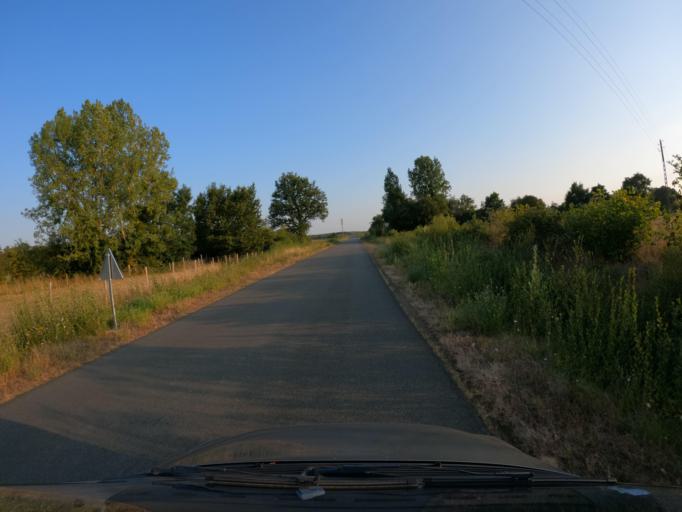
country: FR
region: Pays de la Loire
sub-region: Departement de la Sarthe
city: Brulon
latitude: 47.9141
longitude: -0.2288
